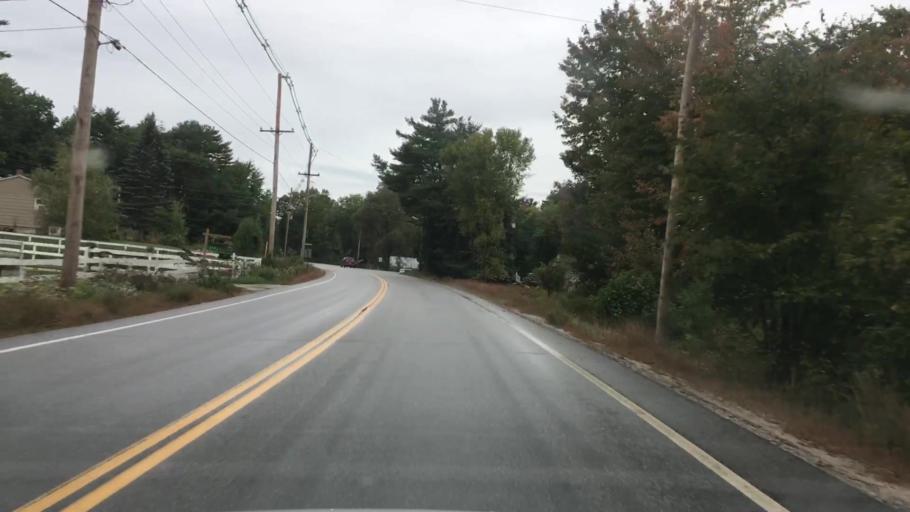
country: US
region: Maine
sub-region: Cumberland County
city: Raymond
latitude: 43.9857
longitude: -70.5556
